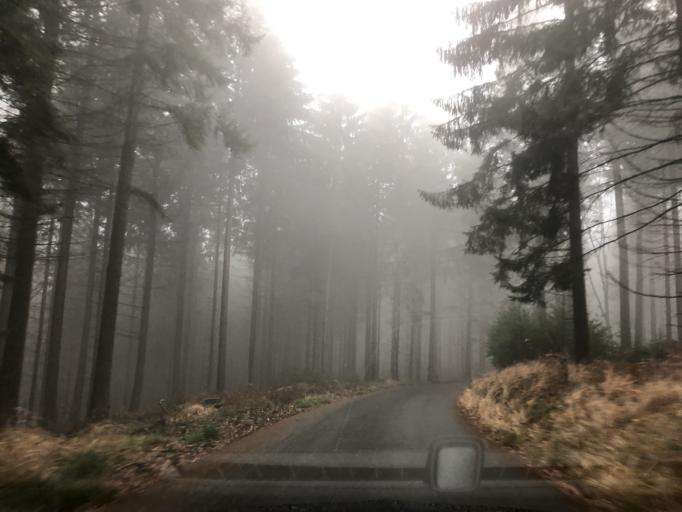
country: DE
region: Baden-Wuerttemberg
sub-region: Karlsruhe Region
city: Wilhelmsfeld
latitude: 49.4522
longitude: 8.7180
